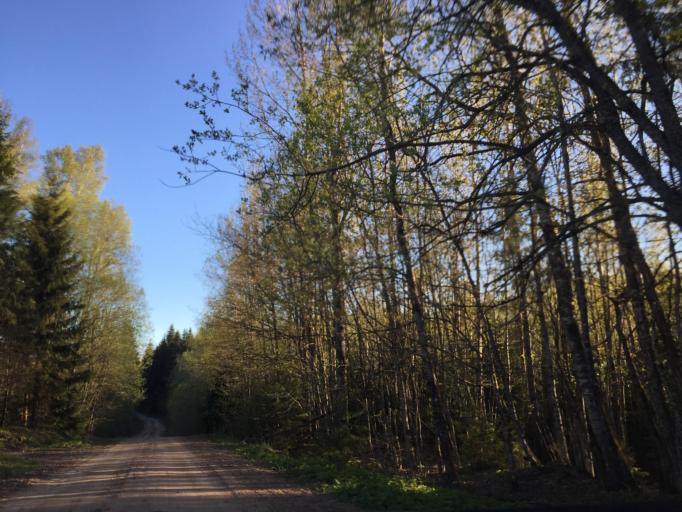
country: LV
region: Vecpiebalga
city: Vecpiebalga
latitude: 56.8554
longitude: 25.9577
